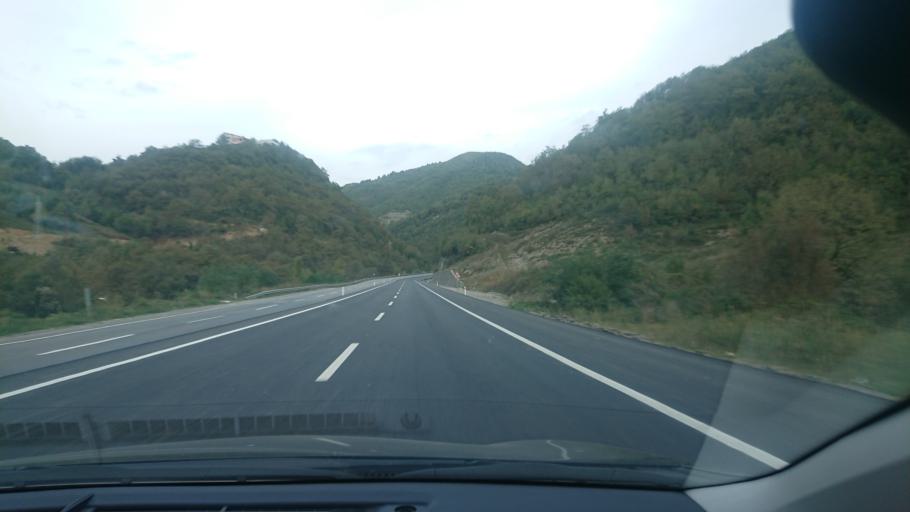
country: TR
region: Zonguldak
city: Beycuma
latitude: 41.3858
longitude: 31.9399
